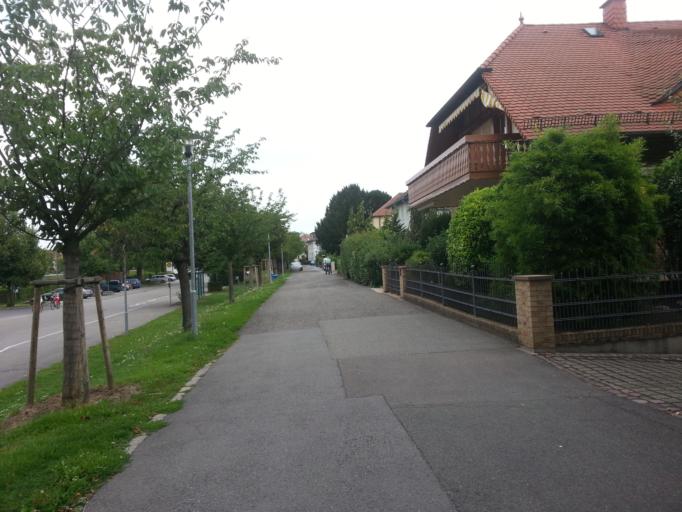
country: DE
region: Baden-Wuerttemberg
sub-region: Karlsruhe Region
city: Ladenburg
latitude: 49.4686
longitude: 8.6065
